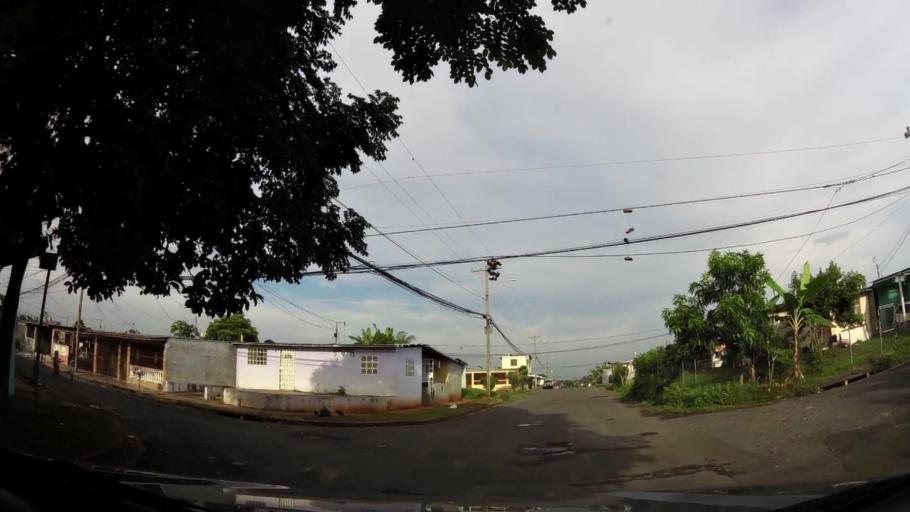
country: PA
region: Panama
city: Tocumen
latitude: 9.0773
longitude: -79.3584
